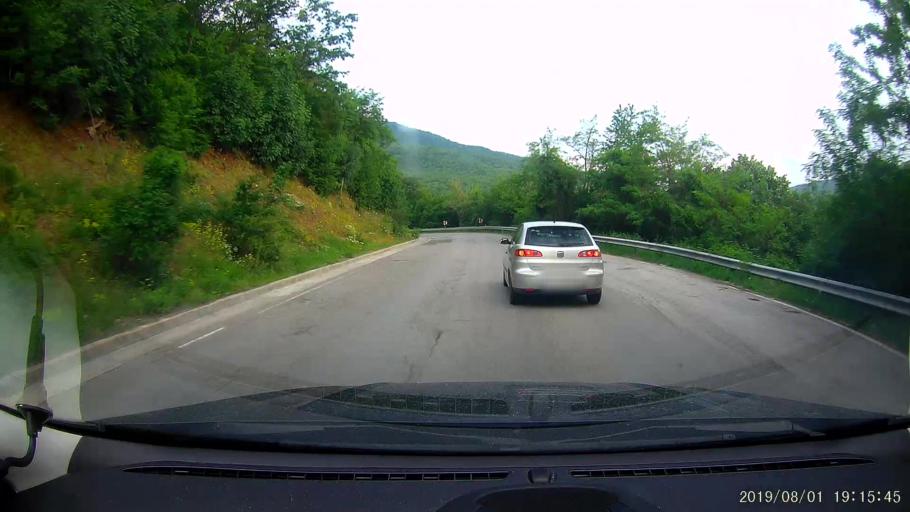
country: BG
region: Shumen
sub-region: Obshtina Smyadovo
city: Smyadovo
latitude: 42.9299
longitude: 26.9443
